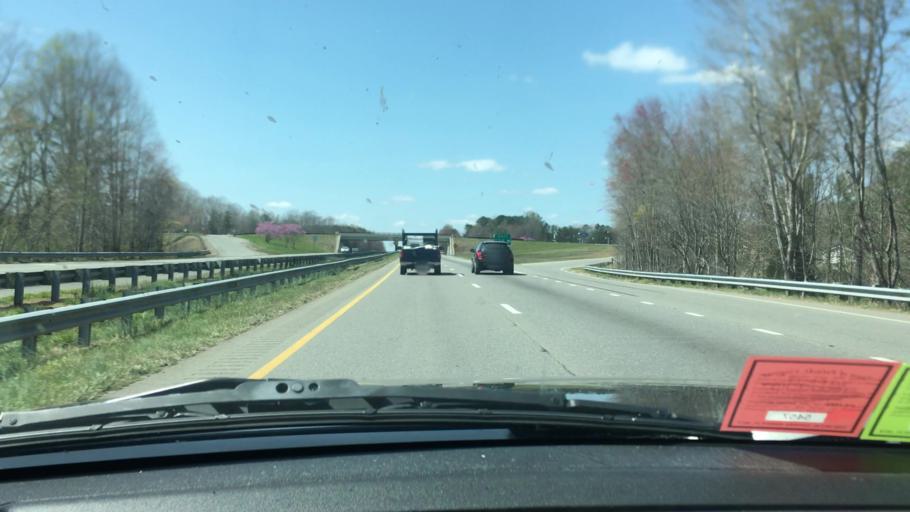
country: US
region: North Carolina
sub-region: Surry County
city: Pilot Mountain
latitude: 36.4059
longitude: -80.4968
